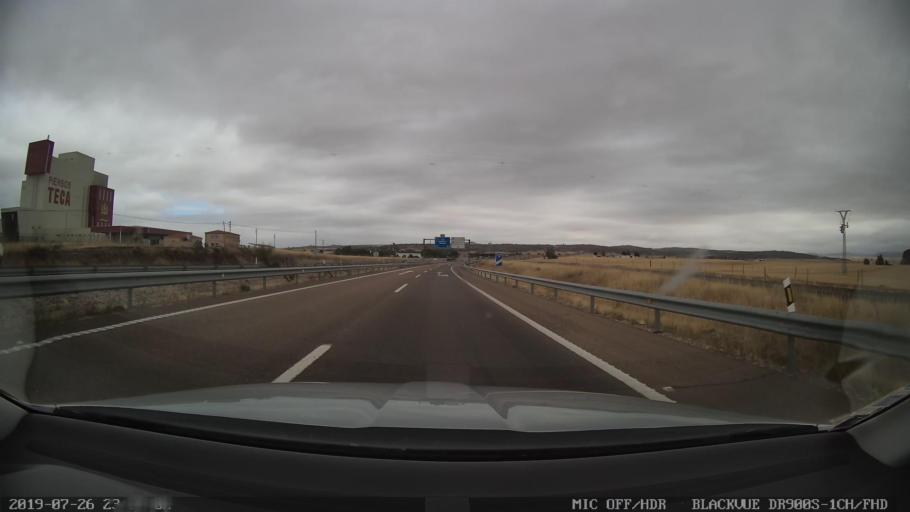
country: ES
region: Extremadura
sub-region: Provincia de Caceres
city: Trujillo
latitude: 39.4056
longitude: -5.8898
